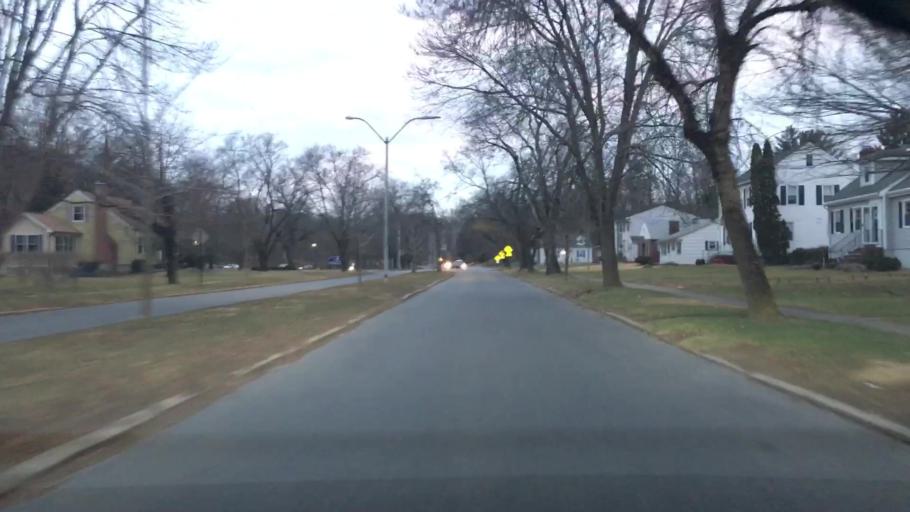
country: US
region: New York
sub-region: Dutchess County
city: Arlington
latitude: 41.6822
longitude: -73.9086
